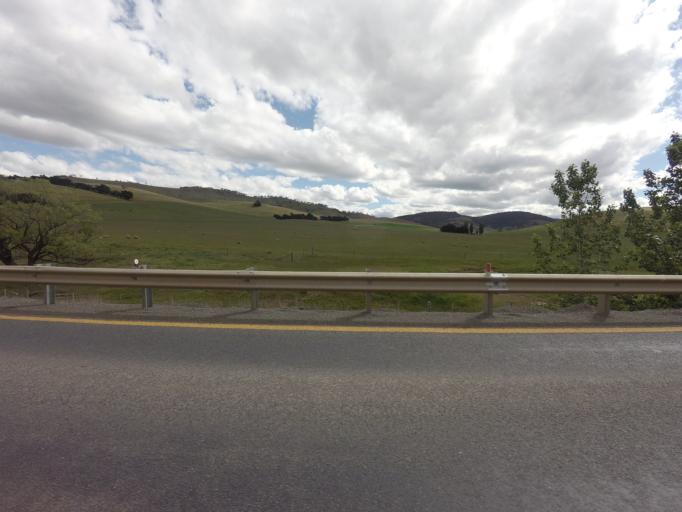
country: AU
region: Tasmania
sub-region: Brighton
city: Bridgewater
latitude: -42.2110
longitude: 147.4064
